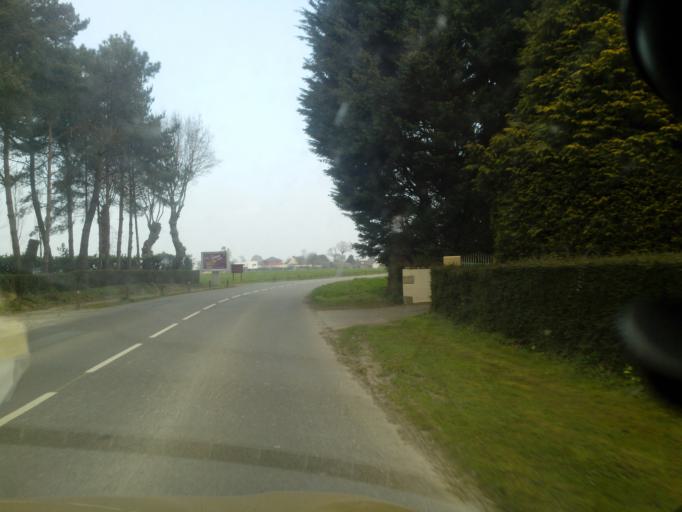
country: FR
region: Brittany
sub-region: Departement d'Ille-et-Vilaine
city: Saint-Meen-le-Grand
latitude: 48.1966
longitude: -2.1824
